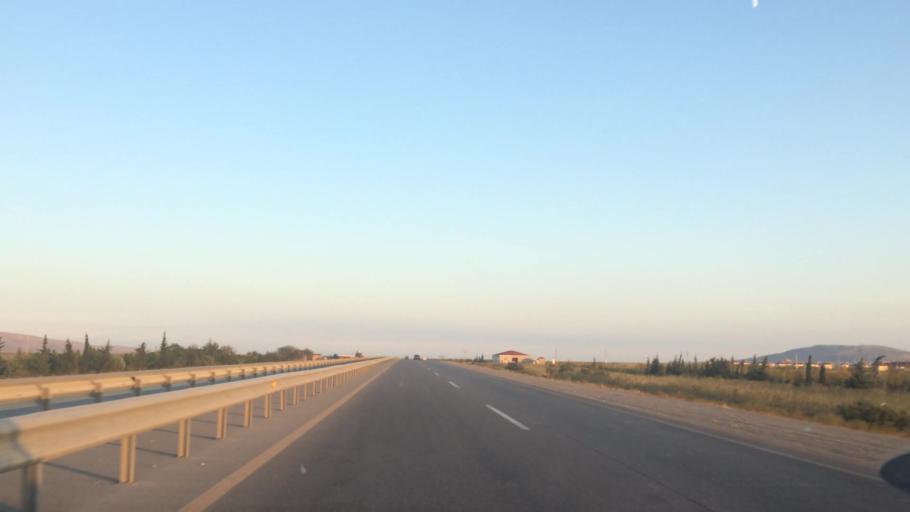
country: AZ
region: Baki
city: Qobustan
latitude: 39.9867
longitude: 49.2069
